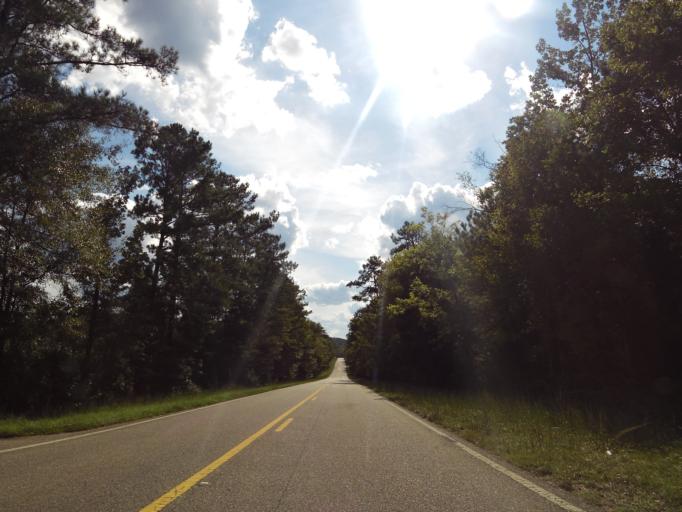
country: US
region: Alabama
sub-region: Dallas County
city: Selmont-West Selmont
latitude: 32.1846
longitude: -87.0395
